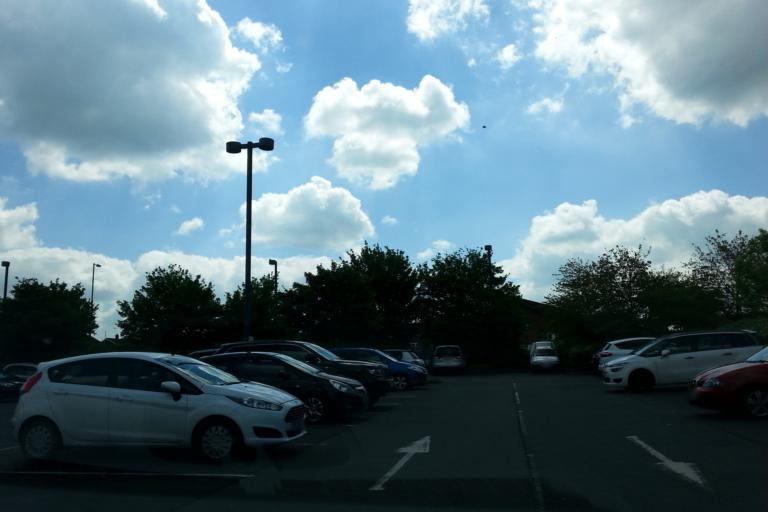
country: GB
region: England
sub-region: Cambridgeshire
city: Yaxley
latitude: 52.5214
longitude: -0.2569
